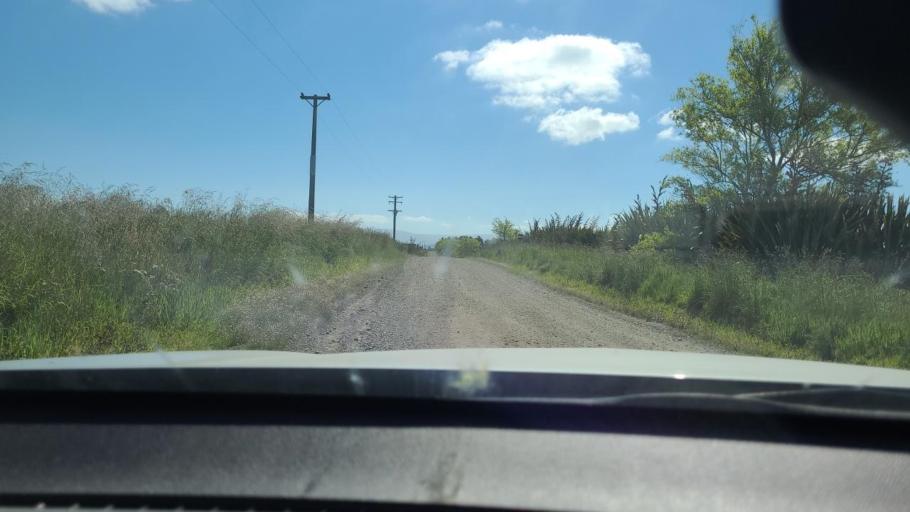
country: NZ
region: Southland
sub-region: Southland District
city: Riverton
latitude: -46.2246
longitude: 168.1354
